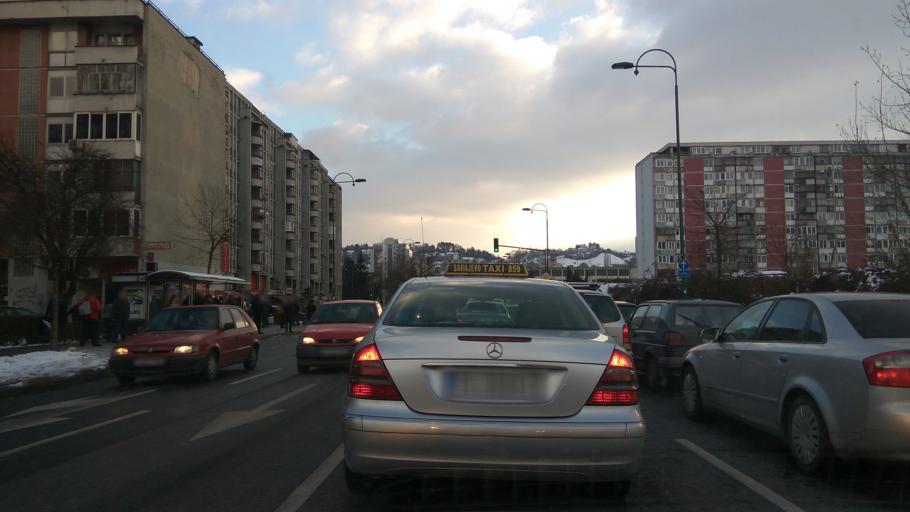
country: BA
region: Federation of Bosnia and Herzegovina
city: Kobilja Glava
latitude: 43.8559
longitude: 18.3919
